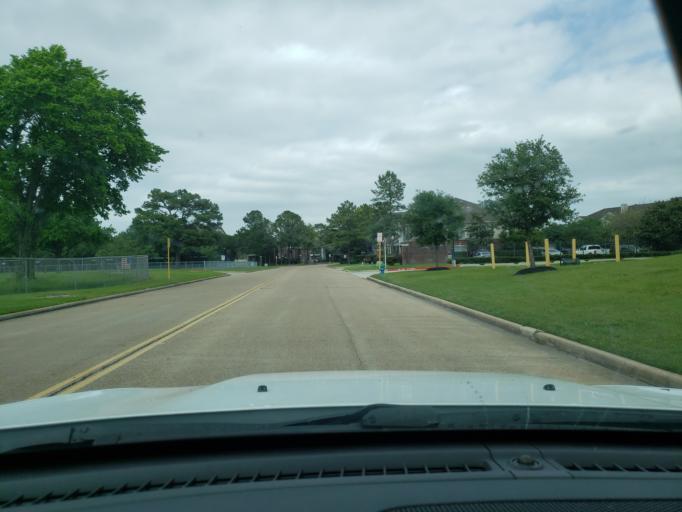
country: US
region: Texas
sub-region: Harris County
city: Jersey Village
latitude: 29.9210
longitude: -95.5594
